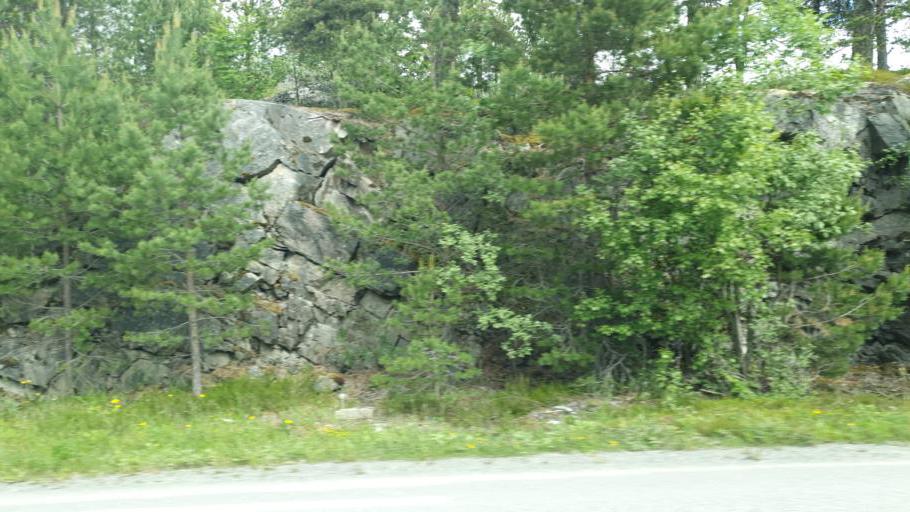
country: NO
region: Sor-Trondelag
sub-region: Trondheim
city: Trondheim
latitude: 63.5755
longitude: 10.3758
